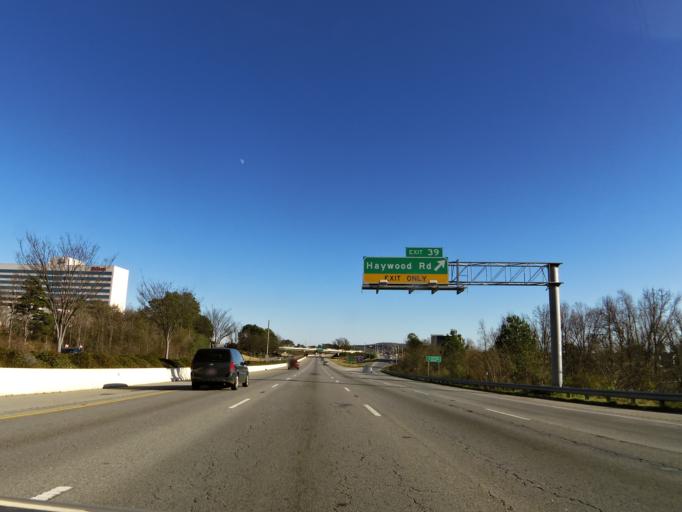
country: US
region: South Carolina
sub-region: Greenville County
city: Wade Hampton
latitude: 34.8559
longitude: -82.3399
